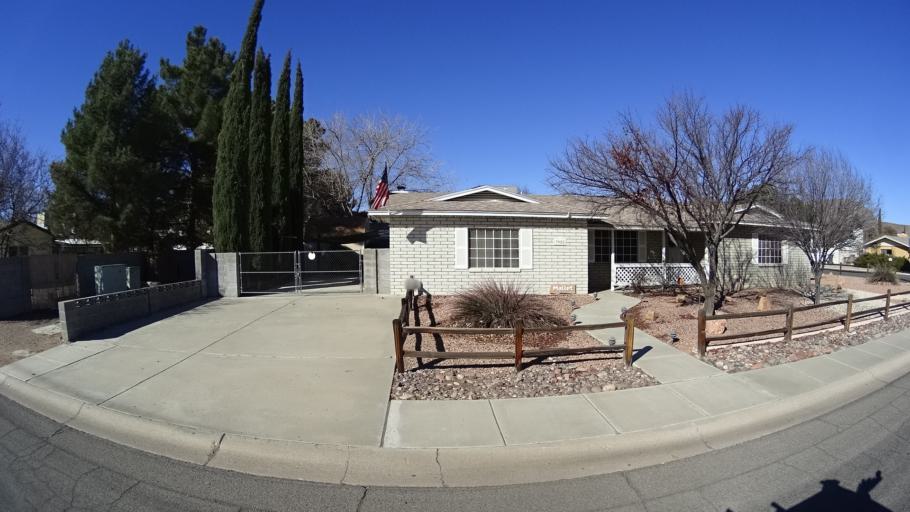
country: US
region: Arizona
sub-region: Mohave County
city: New Kingman-Butler
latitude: 35.2386
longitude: -114.0403
